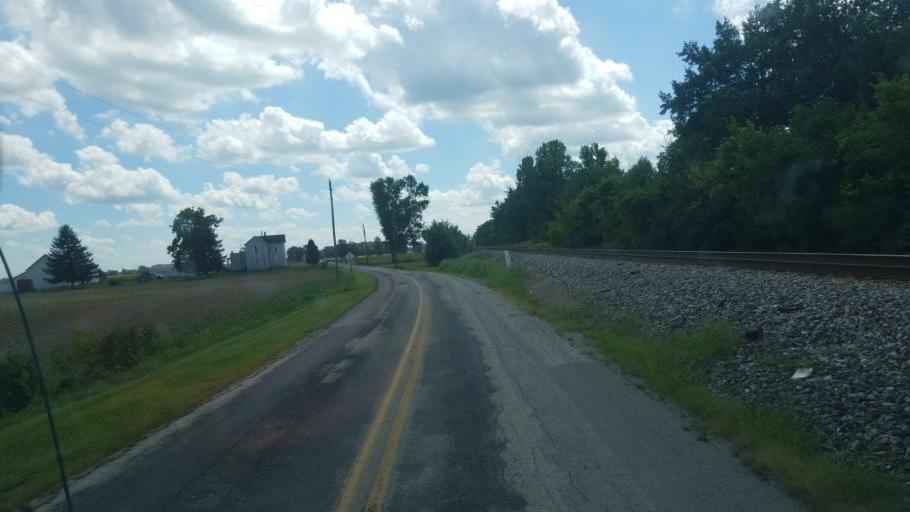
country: US
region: Ohio
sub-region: Marion County
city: Prospect
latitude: 40.4905
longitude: -83.1662
